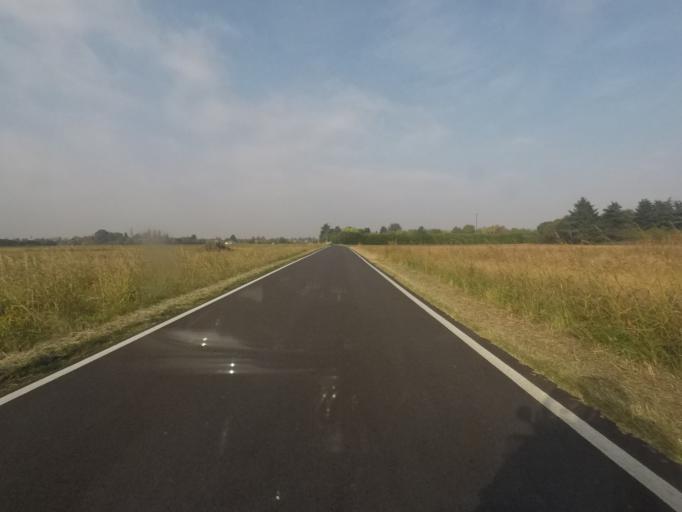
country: IT
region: Lombardy
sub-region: Provincia di Monza e Brianza
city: Villanova
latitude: 45.6278
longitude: 9.3983
